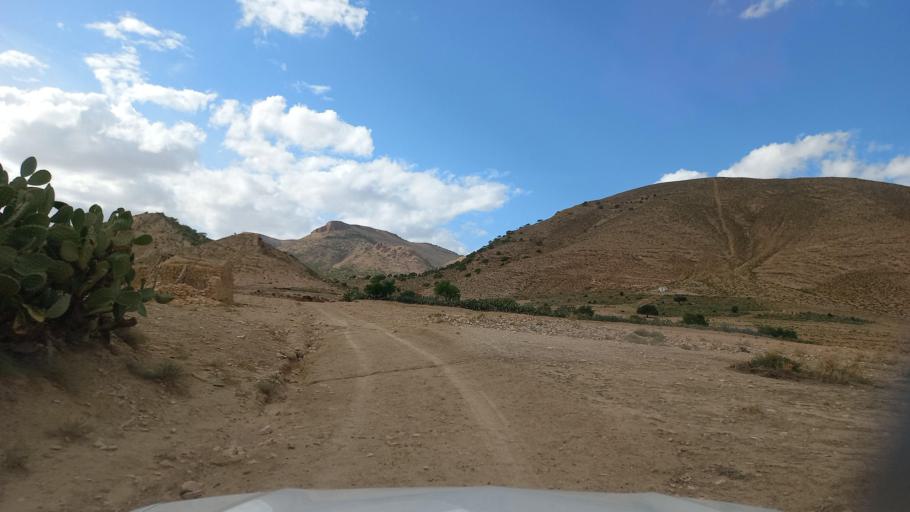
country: TN
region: Al Qasrayn
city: Sbiba
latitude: 35.4526
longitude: 9.0628
